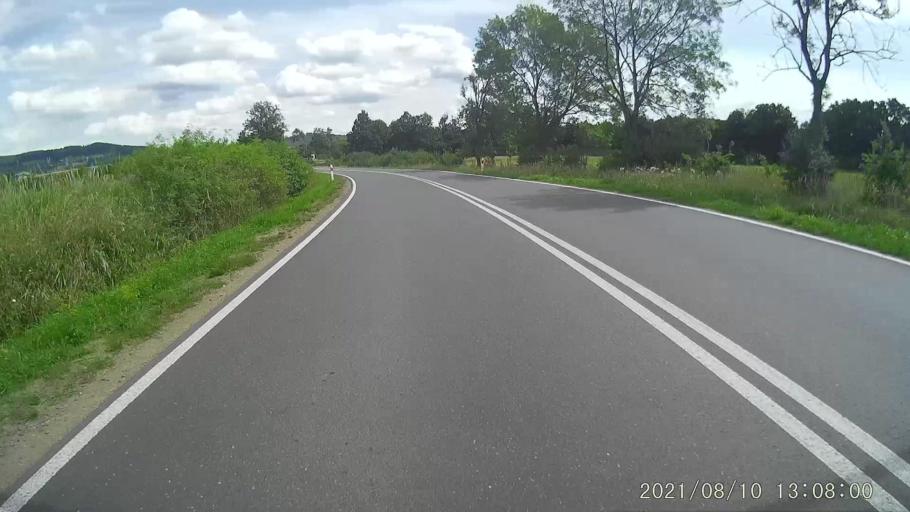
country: PL
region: Lower Silesian Voivodeship
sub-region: Powiat klodzki
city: Bozkow
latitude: 50.4902
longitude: 16.5652
